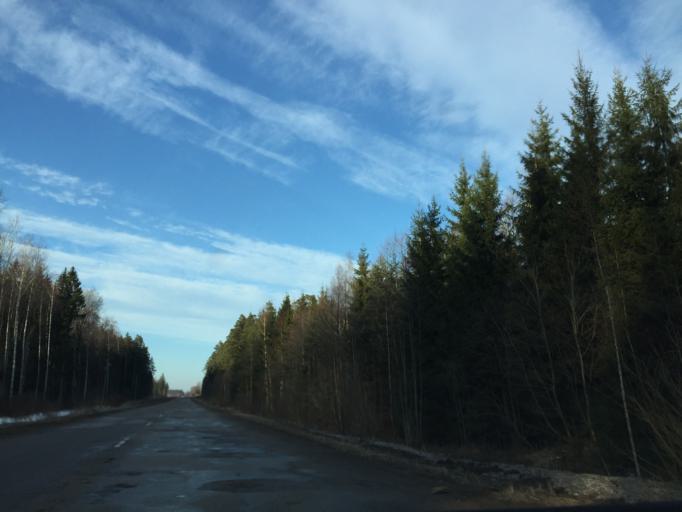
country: LV
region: Lecava
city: Iecava
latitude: 56.7205
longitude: 24.1113
